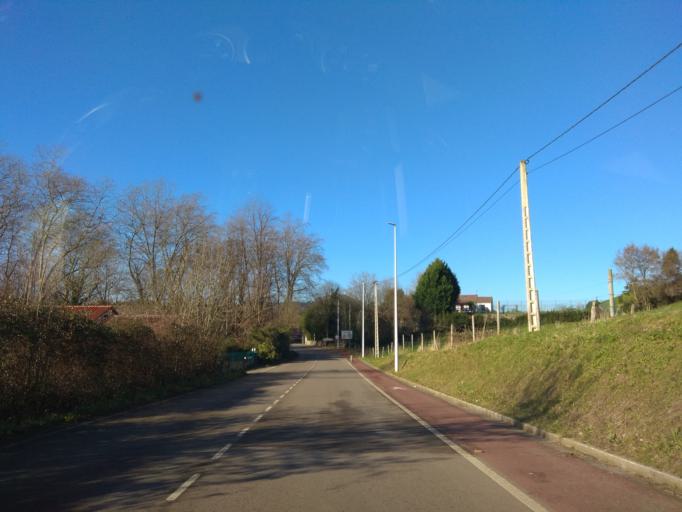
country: ES
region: Cantabria
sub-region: Provincia de Cantabria
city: Entrambasaguas
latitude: 43.3723
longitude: -3.6698
